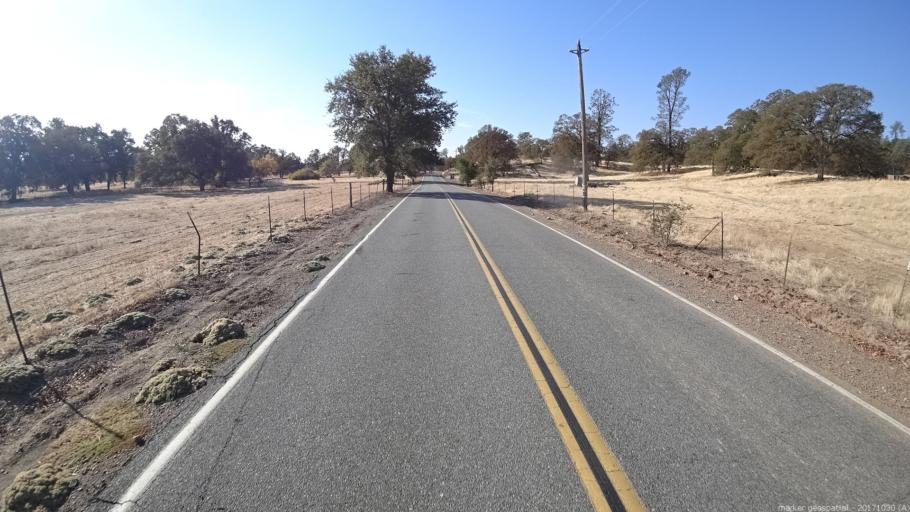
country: US
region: California
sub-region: Shasta County
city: Palo Cedro
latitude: 40.5900
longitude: -122.1745
